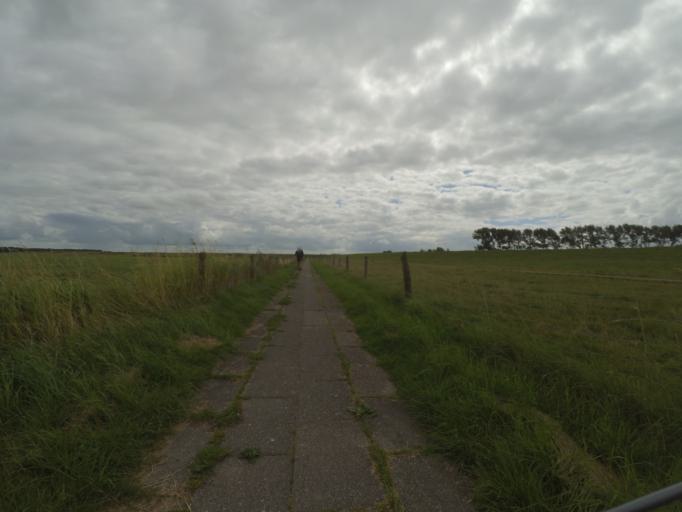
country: NL
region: Friesland
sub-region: Gemeente Dongeradeel
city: Anjum
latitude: 53.3381
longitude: 6.1539
